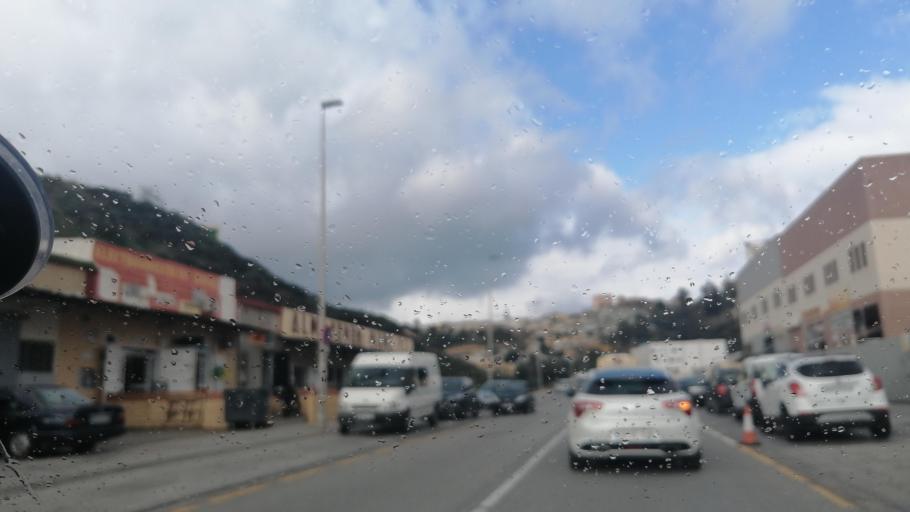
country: ES
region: Ceuta
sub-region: Ceuta
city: Ceuta
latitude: 35.8804
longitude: -5.3375
